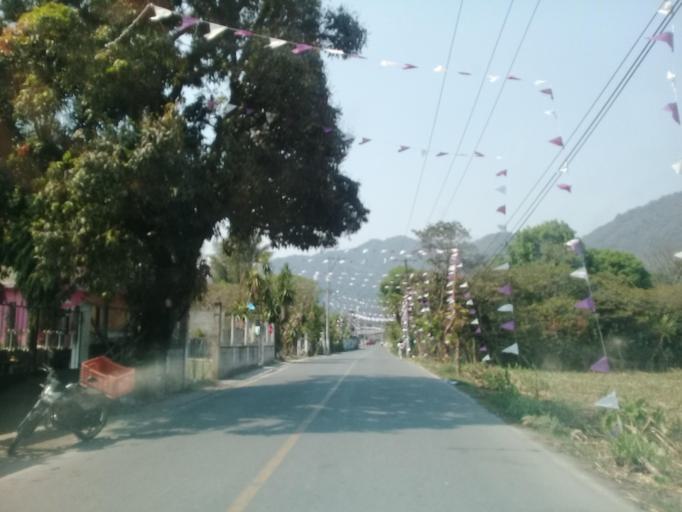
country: MX
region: Veracruz
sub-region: Ixtaczoquitlan
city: Campo Chico
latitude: 18.8278
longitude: -97.0214
